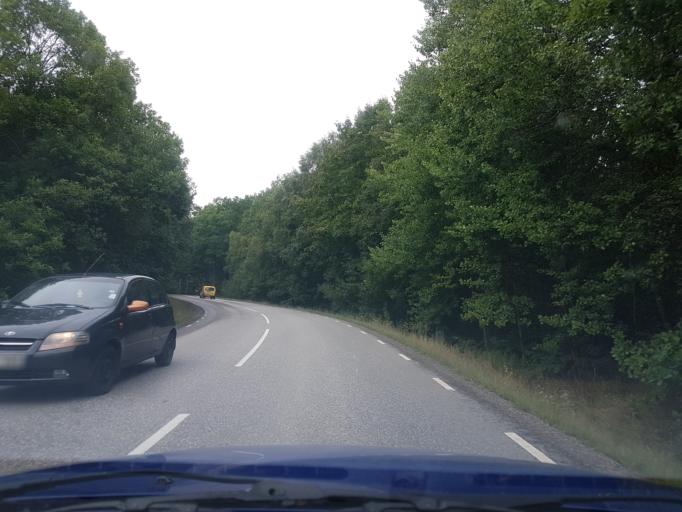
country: SE
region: Vaestra Goetaland
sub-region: Ale Kommun
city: Salanda
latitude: 57.9400
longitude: 12.2217
